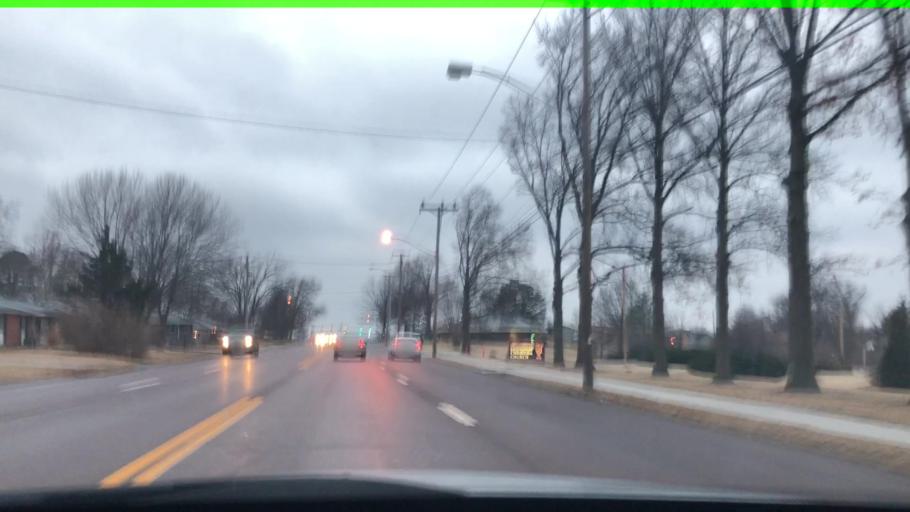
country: US
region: Missouri
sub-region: Boone County
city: Columbia
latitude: 38.9545
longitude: -92.3770
